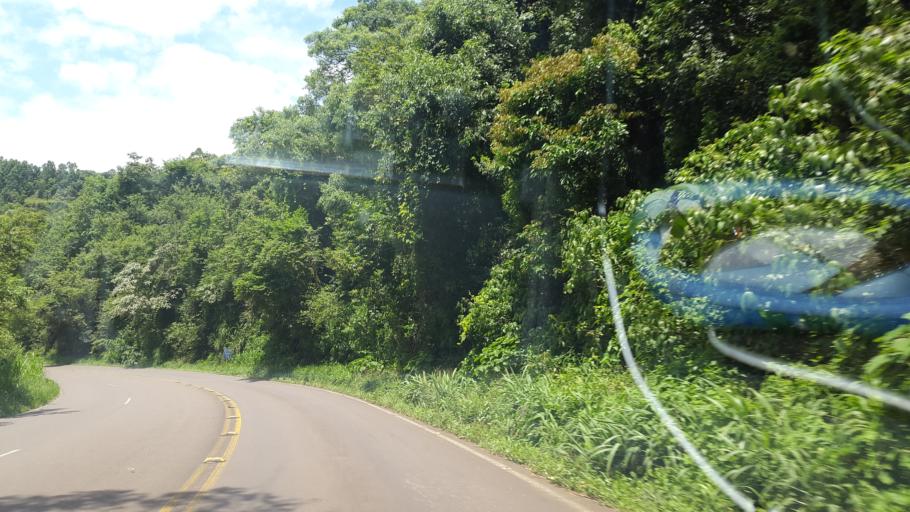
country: BR
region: Rio Grande do Sul
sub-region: Frederico Westphalen
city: Frederico Westphalen
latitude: -27.0632
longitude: -53.4745
